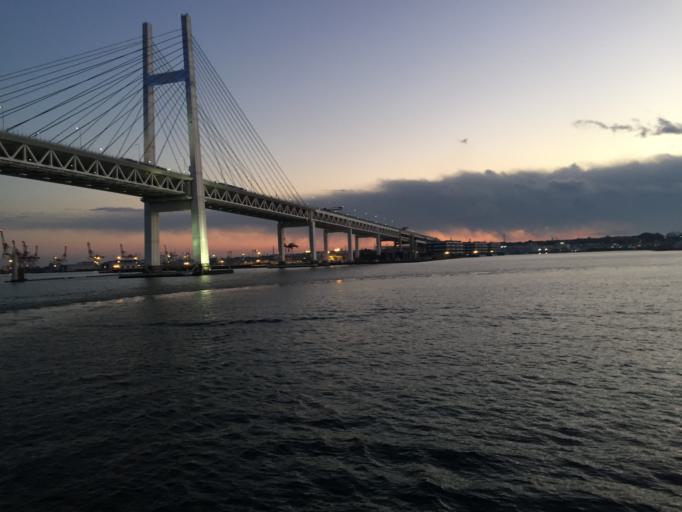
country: JP
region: Kanagawa
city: Yokohama
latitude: 35.4566
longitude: 139.6722
